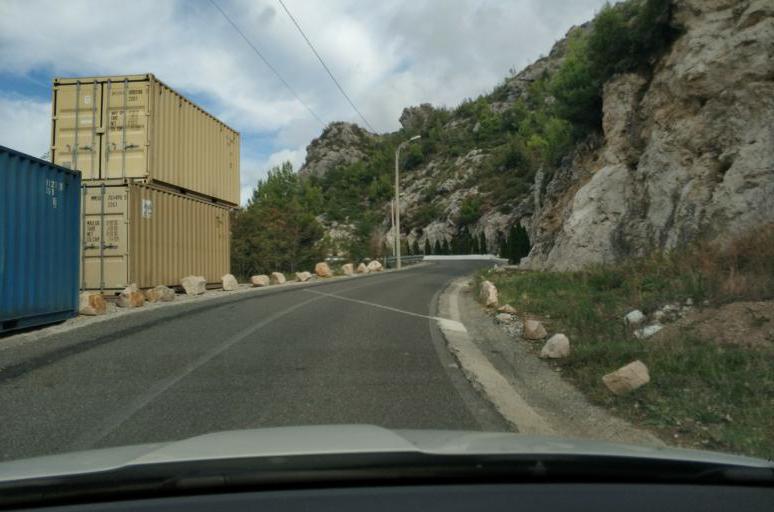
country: AL
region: Durres
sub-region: Rrethi i Krujes
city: Kruje
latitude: 41.5229
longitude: 19.7934
